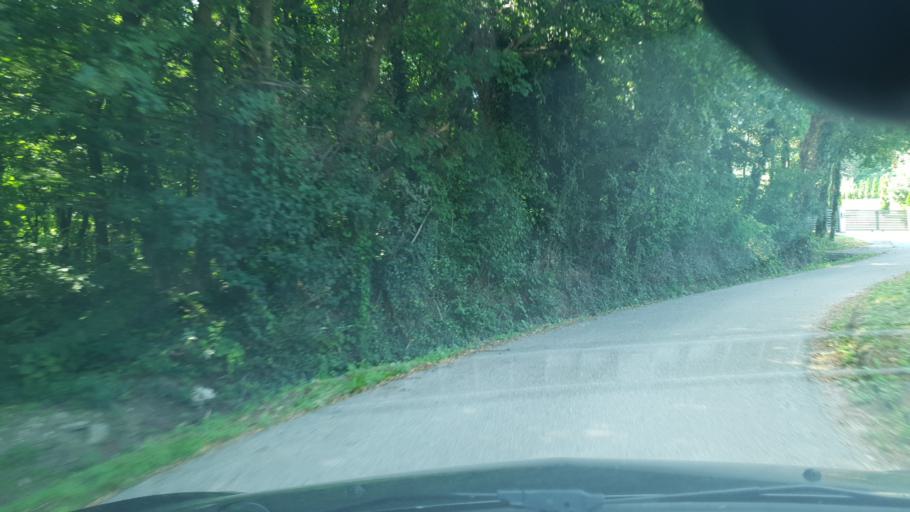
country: HR
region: Grad Zagreb
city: Stenjevec
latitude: 45.8405
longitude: 15.9091
